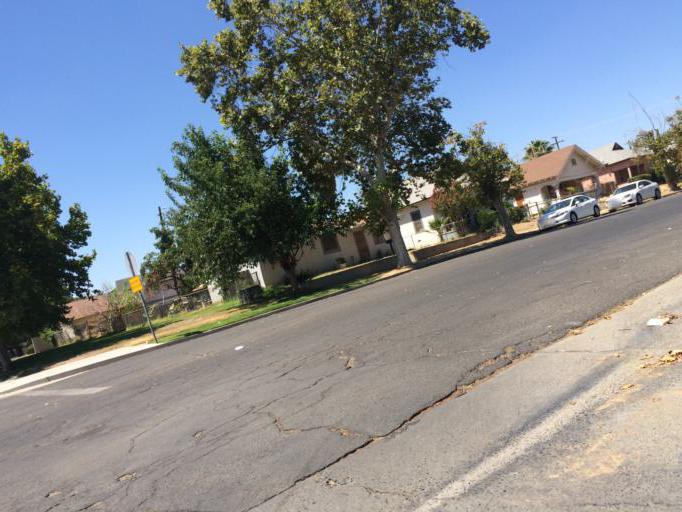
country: US
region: California
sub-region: Fresno County
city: Fresno
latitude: 36.7224
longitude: -119.7967
